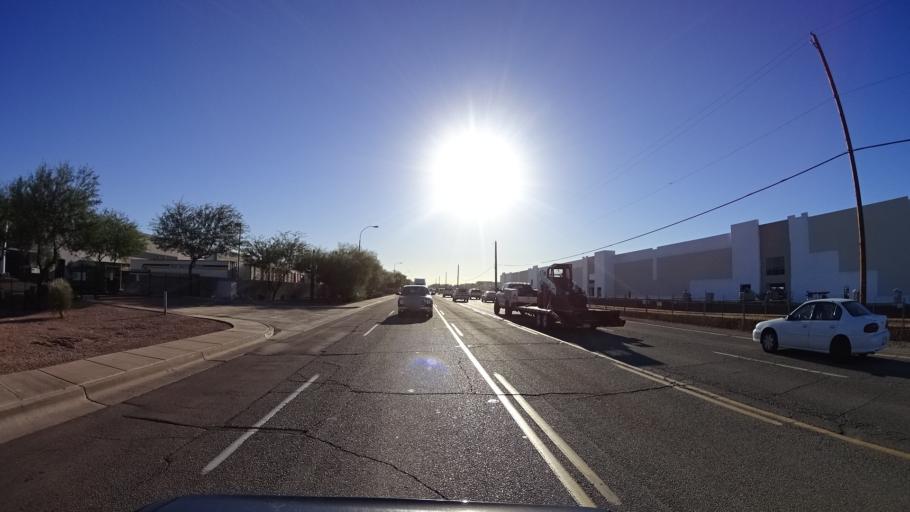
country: US
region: Arizona
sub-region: Maricopa County
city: Tolleson
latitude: 33.4372
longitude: -112.2159
